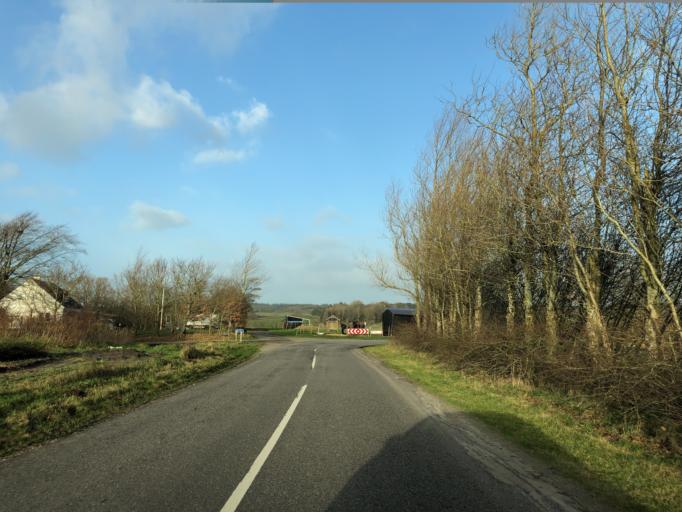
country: DK
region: Central Jutland
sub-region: Ringkobing-Skjern Kommune
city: Videbaek
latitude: 56.1937
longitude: 8.5421
